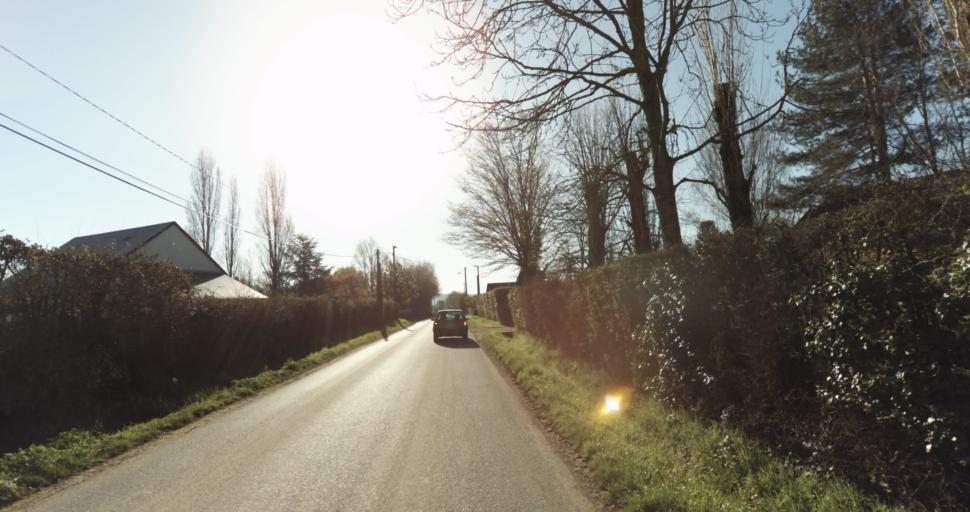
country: FR
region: Lower Normandy
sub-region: Departement du Calvados
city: Saint-Pierre-sur-Dives
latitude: 49.0044
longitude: -0.0077
